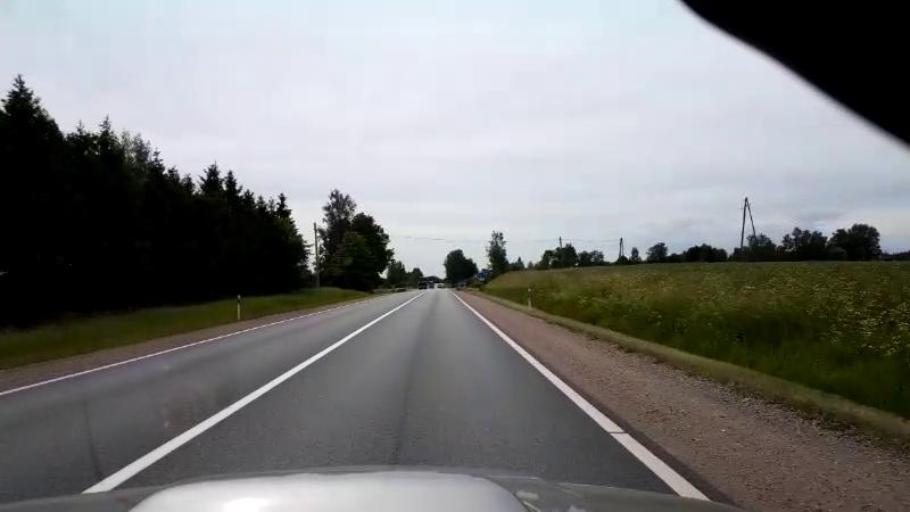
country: LV
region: Bauskas Rajons
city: Bauska
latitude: 56.4930
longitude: 24.1761
